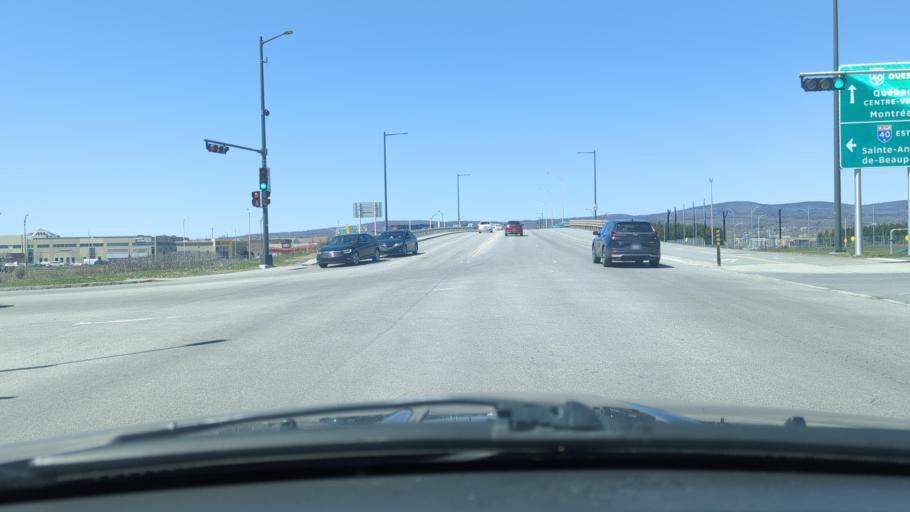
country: CA
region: Quebec
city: Quebec
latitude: 46.8603
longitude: -71.2111
